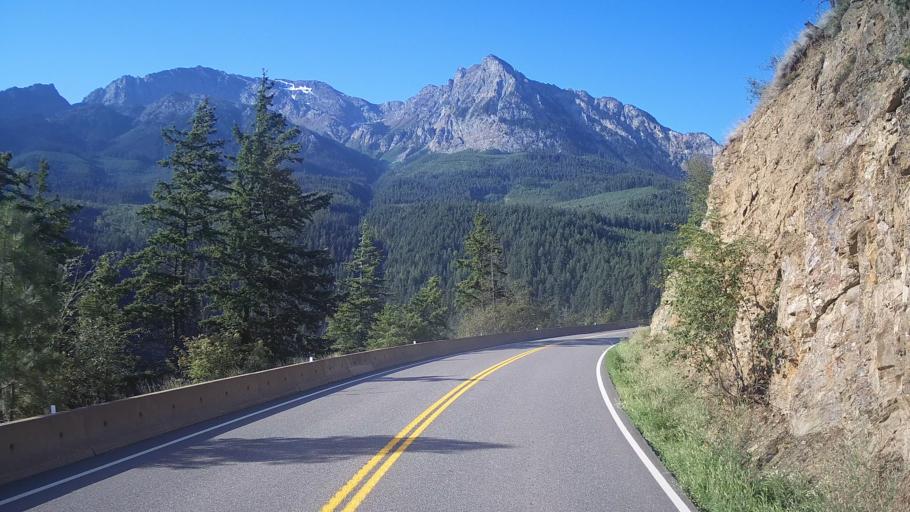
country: CA
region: British Columbia
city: Lillooet
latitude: 50.6544
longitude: -122.0023
